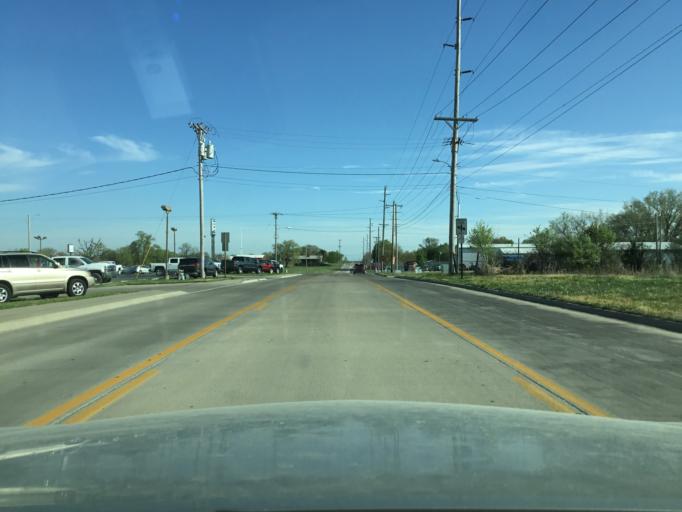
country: US
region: Kansas
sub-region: Neosho County
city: Chanute
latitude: 37.6879
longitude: -95.4710
